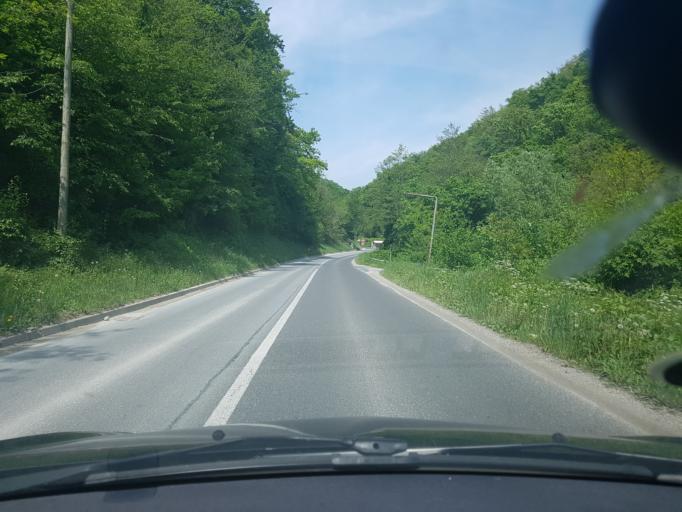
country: HR
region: Krapinsko-Zagorska
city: Pregrada
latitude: 46.1732
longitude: 15.7541
